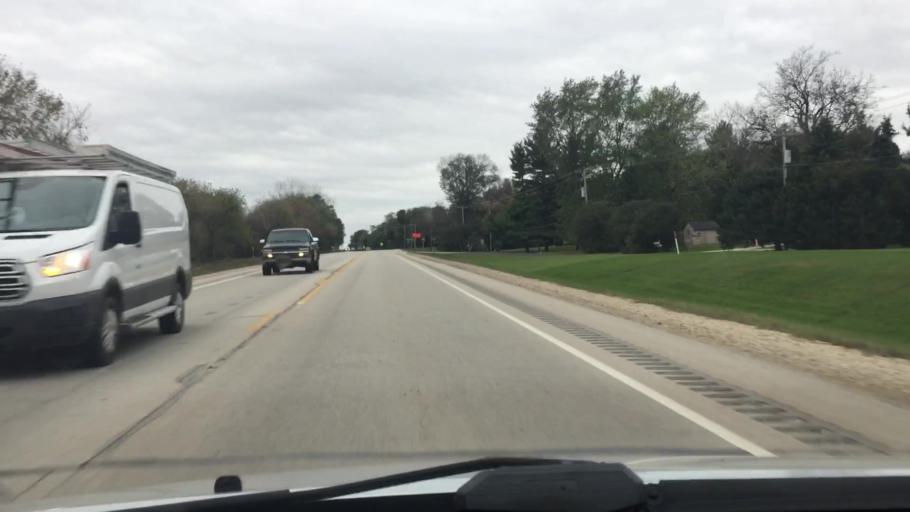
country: US
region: Wisconsin
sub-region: Waukesha County
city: Waukesha
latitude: 42.9777
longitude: -88.2838
